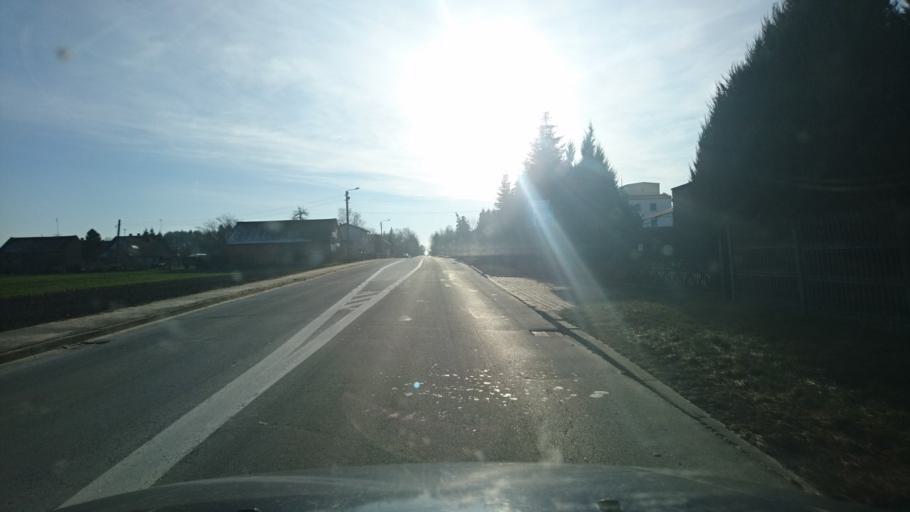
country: PL
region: Opole Voivodeship
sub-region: Powiat oleski
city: Dalachow
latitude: 51.0766
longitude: 18.6028
